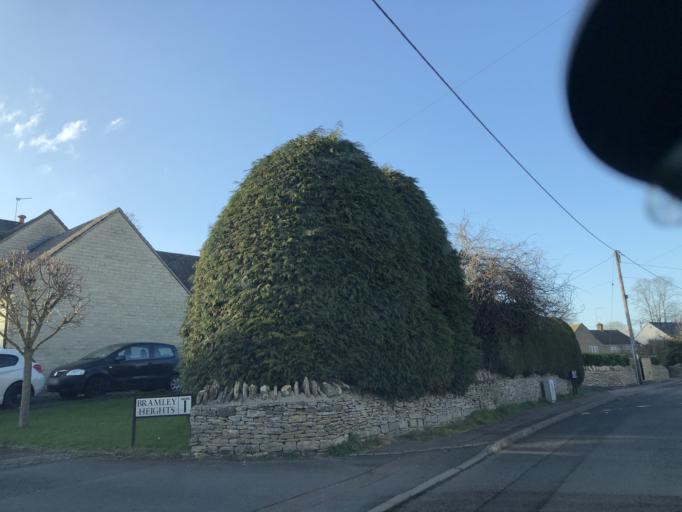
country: GB
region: England
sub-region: Oxfordshire
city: Witney
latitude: 51.7840
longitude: -1.4974
